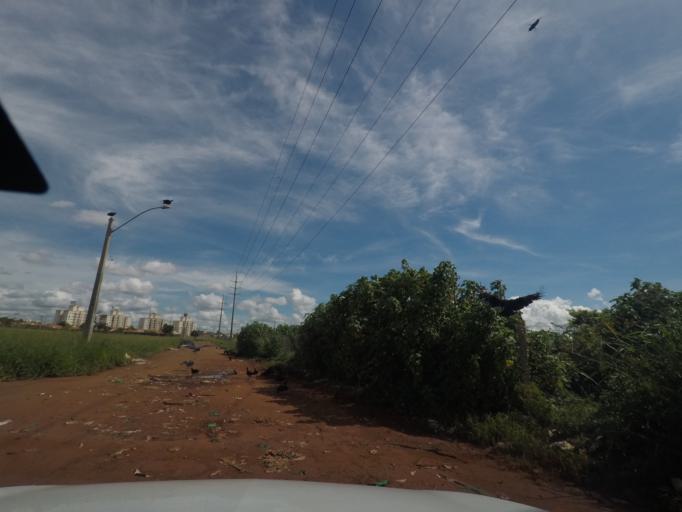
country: BR
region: Goias
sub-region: Goiania
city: Goiania
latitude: -16.7157
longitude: -49.3489
